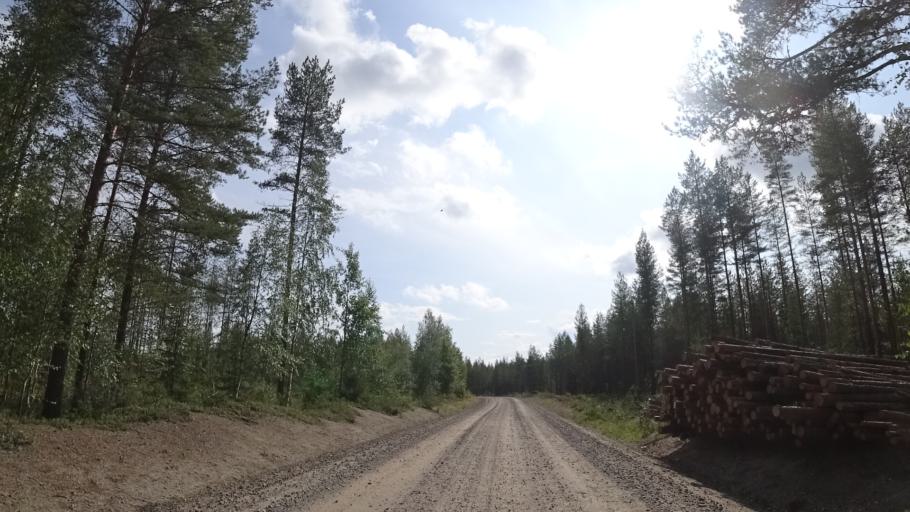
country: FI
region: North Karelia
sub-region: Pielisen Karjala
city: Lieksa
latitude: 63.5550
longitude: 30.0632
